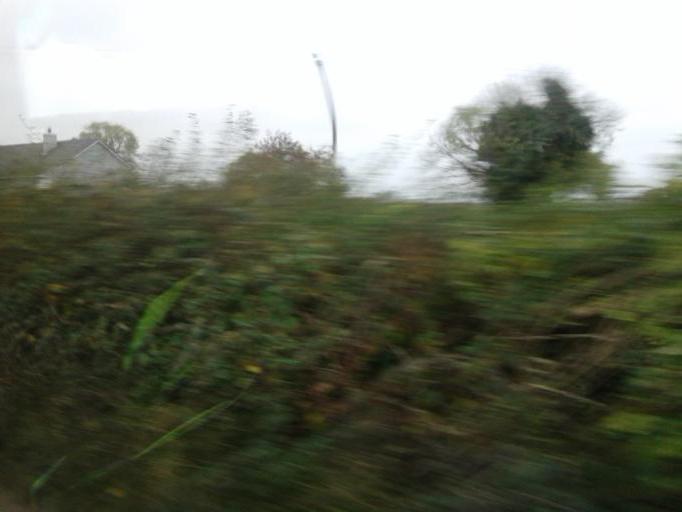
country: IE
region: Leinster
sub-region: Uibh Fhaili
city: Birr
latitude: 52.9569
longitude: -8.0271
